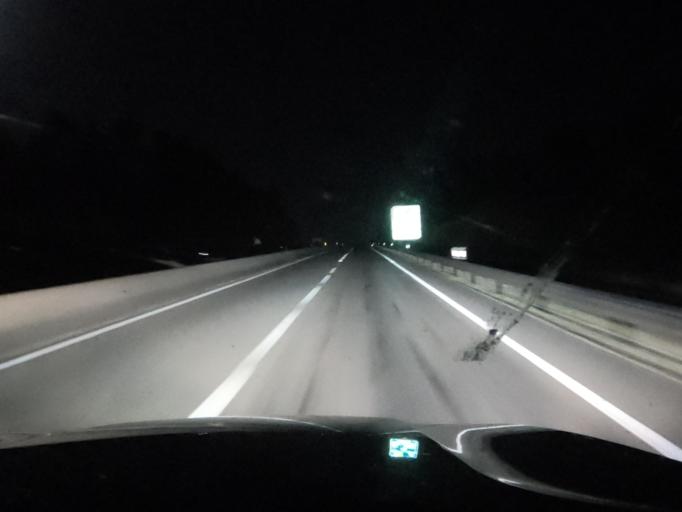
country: PT
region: Viseu
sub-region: Concelho de Tondela
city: Tondela
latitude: 40.5950
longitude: -8.0015
